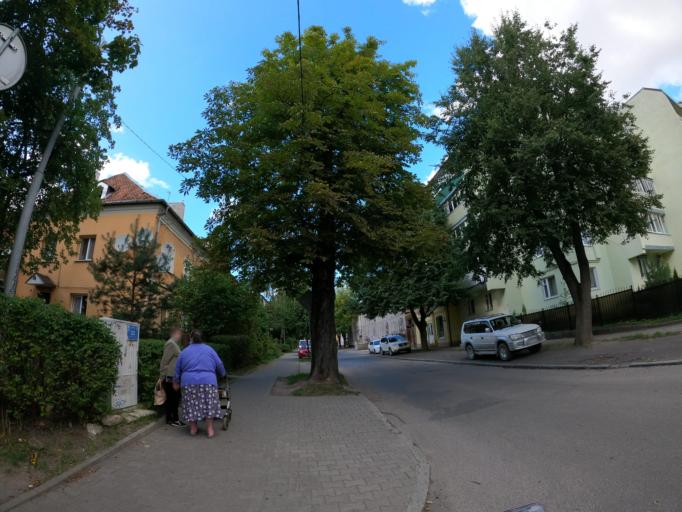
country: RU
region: Kaliningrad
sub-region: Gorod Kaliningrad
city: Kaliningrad
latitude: 54.7304
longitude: 20.4743
